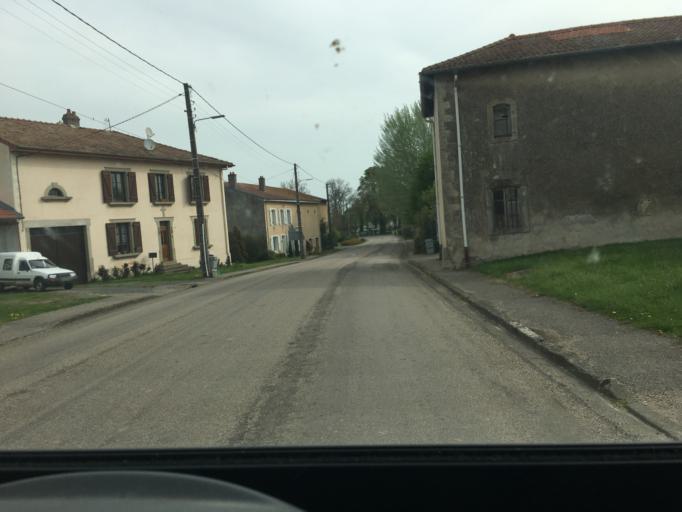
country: FR
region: Lorraine
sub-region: Departement de la Moselle
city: Vic-sur-Seille
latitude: 48.7246
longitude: 6.5362
